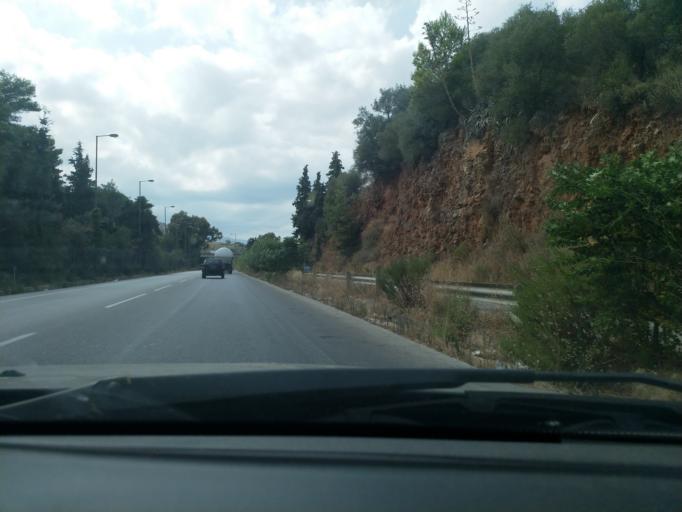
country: GR
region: Crete
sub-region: Nomos Chanias
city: Georgioupolis
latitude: 35.3574
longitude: 24.2659
